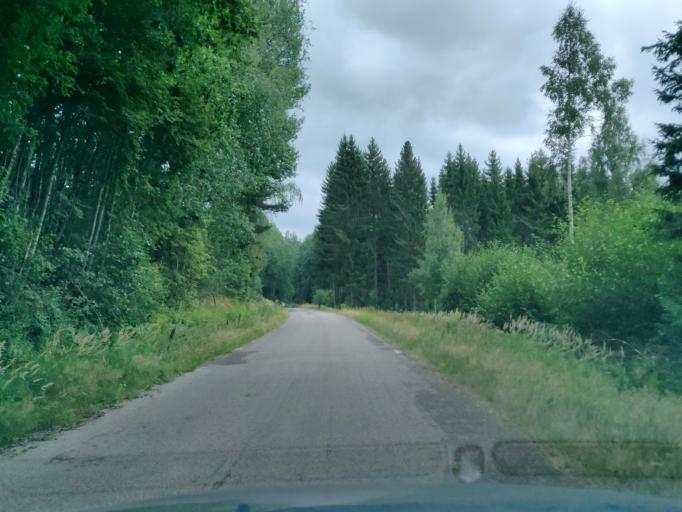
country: SE
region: Vaermland
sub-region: Munkfors Kommun
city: Munkfors
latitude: 59.9151
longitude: 13.5657
